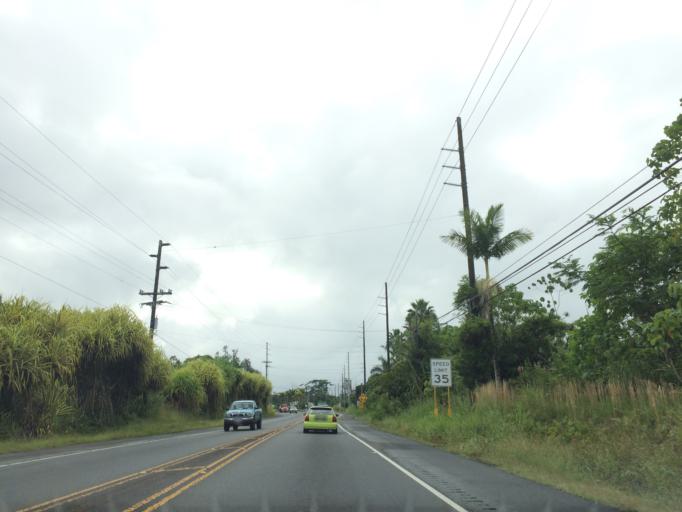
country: US
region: Hawaii
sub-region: Hawaii County
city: Hawaiian Paradise Park
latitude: 19.5076
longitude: -154.9581
